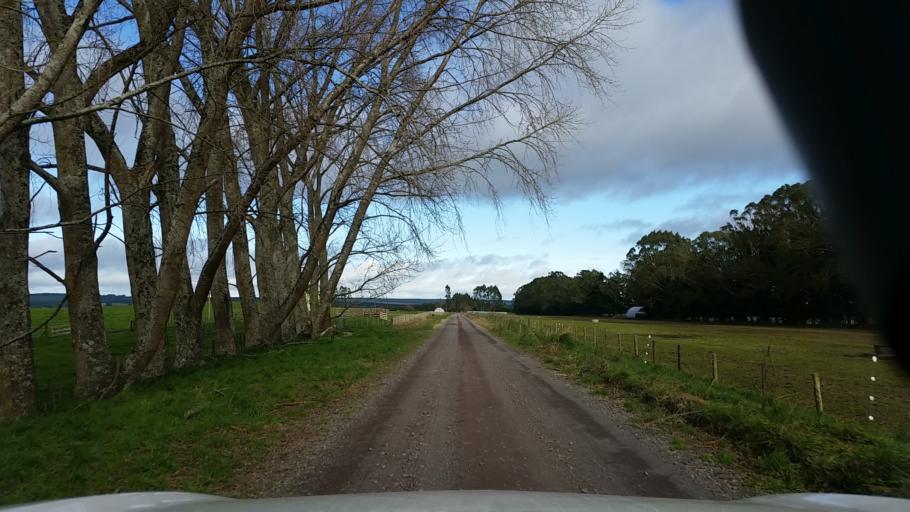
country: NZ
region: Bay of Plenty
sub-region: Whakatane District
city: Murupara
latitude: -38.4720
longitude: 176.4166
